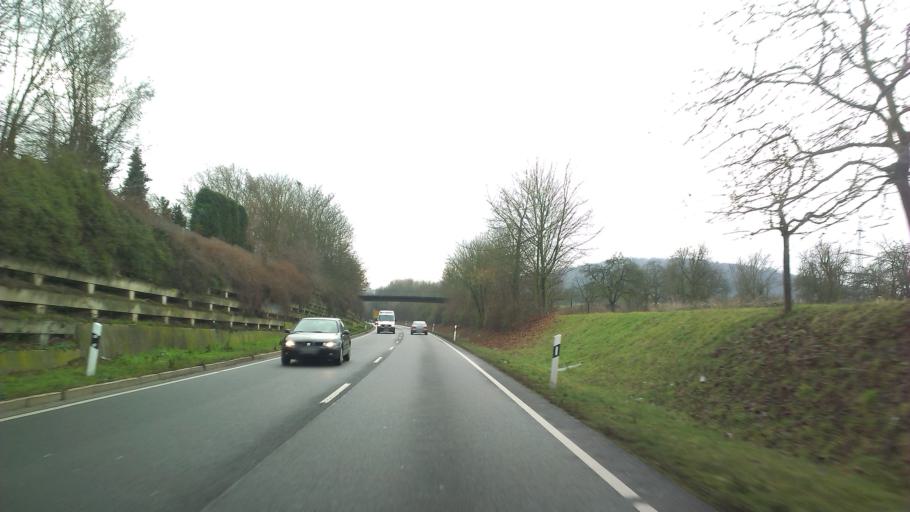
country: DE
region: Baden-Wuerttemberg
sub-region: Karlsruhe Region
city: Rauenberg
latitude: 49.2678
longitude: 8.6967
